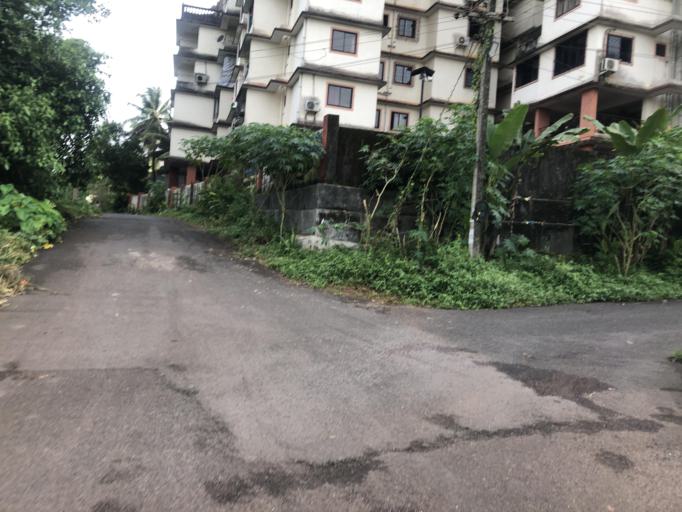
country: IN
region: Goa
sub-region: North Goa
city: Serula
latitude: 15.5463
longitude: 73.8256
